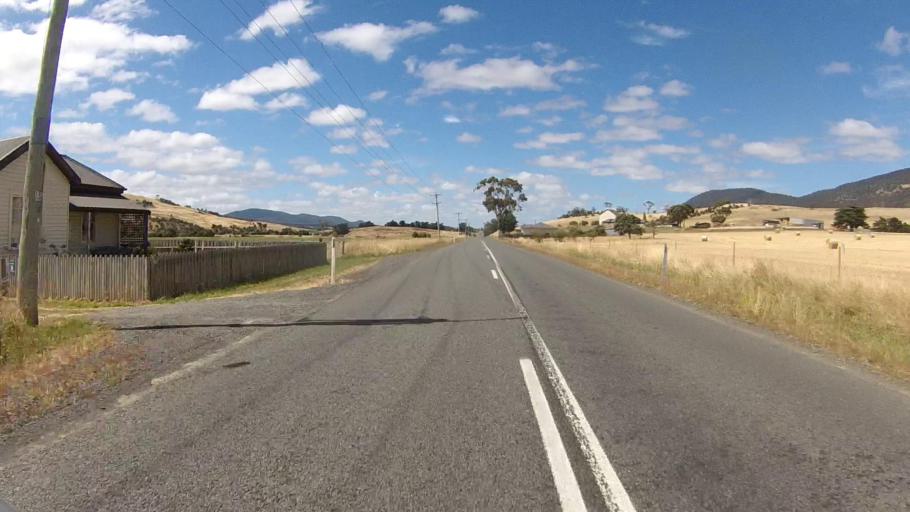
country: AU
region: Tasmania
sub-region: Brighton
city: Bridgewater
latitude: -42.5904
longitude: 147.4101
